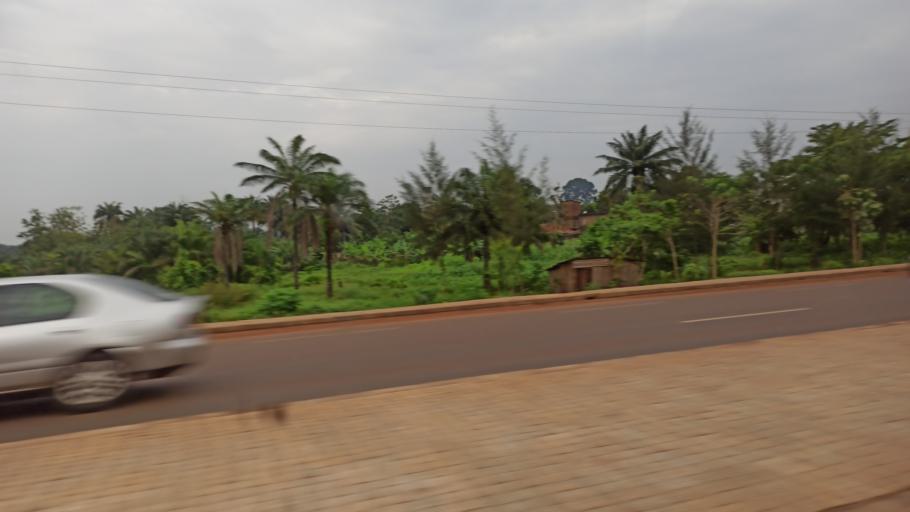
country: BJ
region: Queme
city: Porto-Novo
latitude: 6.5323
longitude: 2.5992
